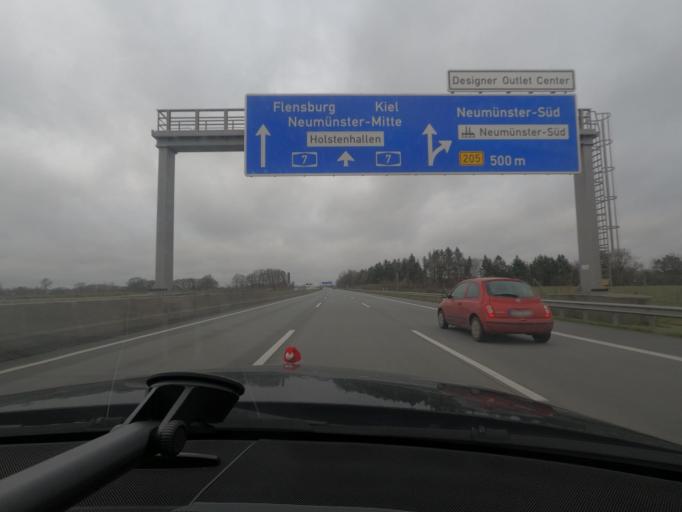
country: DE
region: Schleswig-Holstein
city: Padenstedt
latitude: 54.0360
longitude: 9.9319
